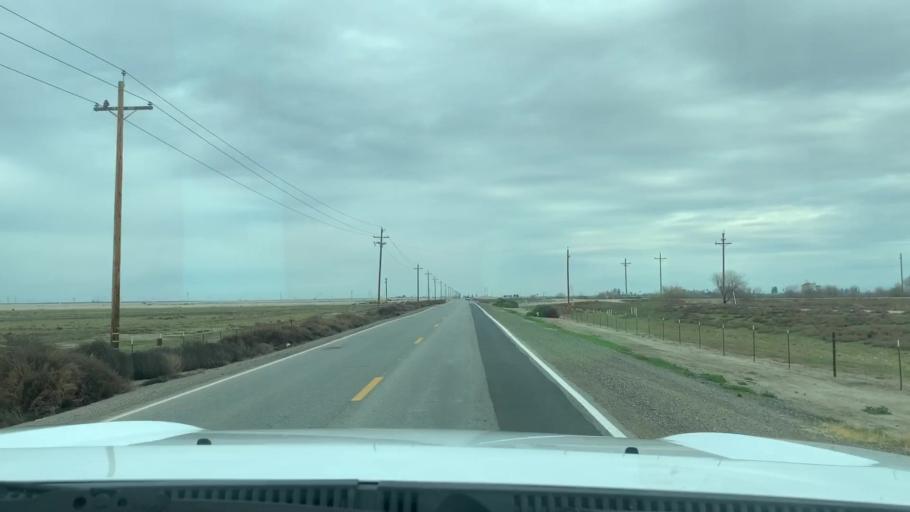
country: US
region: California
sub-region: Kern County
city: Rosedale
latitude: 35.3368
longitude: -119.2523
